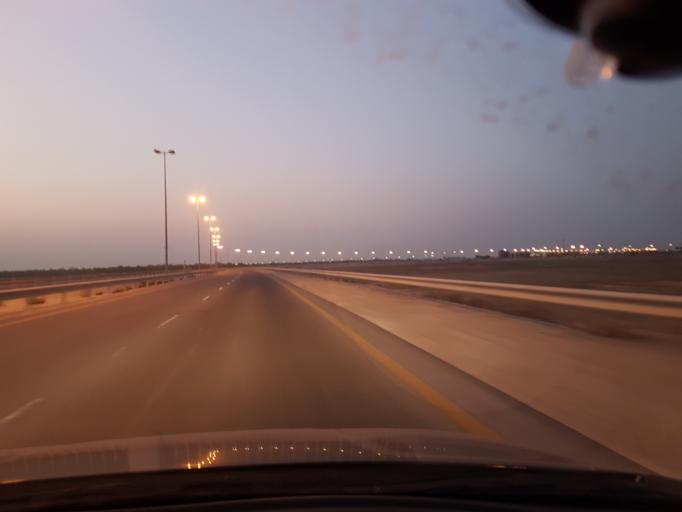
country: BH
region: Central Governorate
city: Dar Kulayb
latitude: 26.0072
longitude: 50.4847
